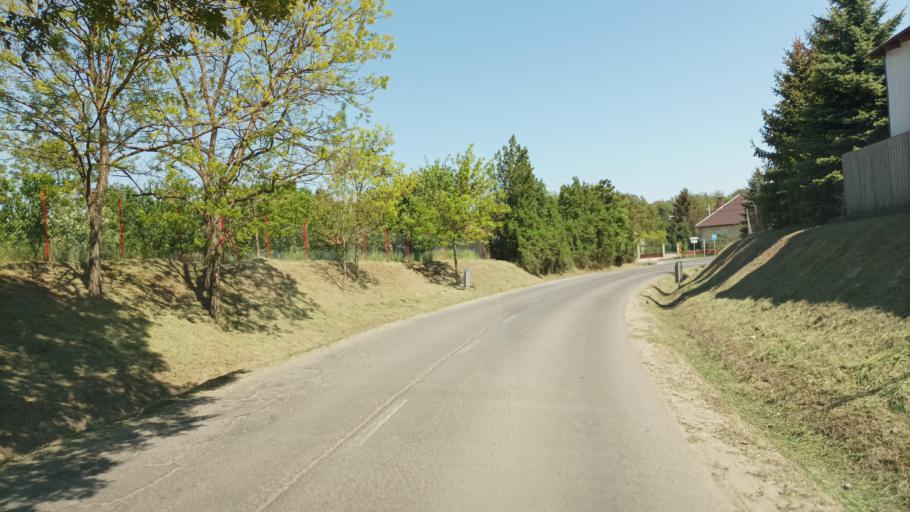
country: HU
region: Pest
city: Suelysap
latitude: 47.4505
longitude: 19.5156
